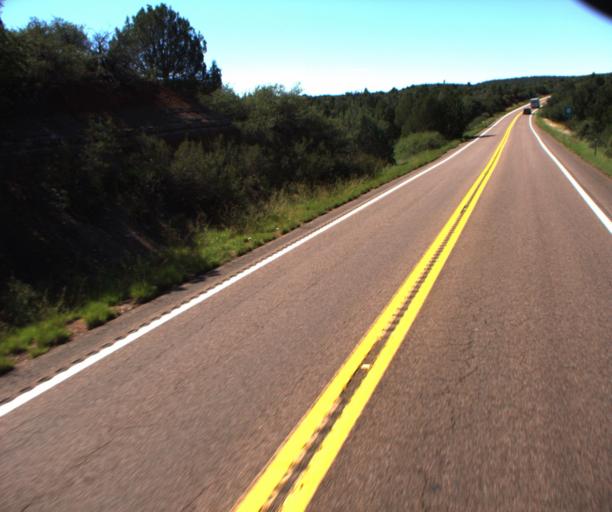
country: US
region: Arizona
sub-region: Navajo County
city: Cibecue
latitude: 34.0094
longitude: -110.2522
